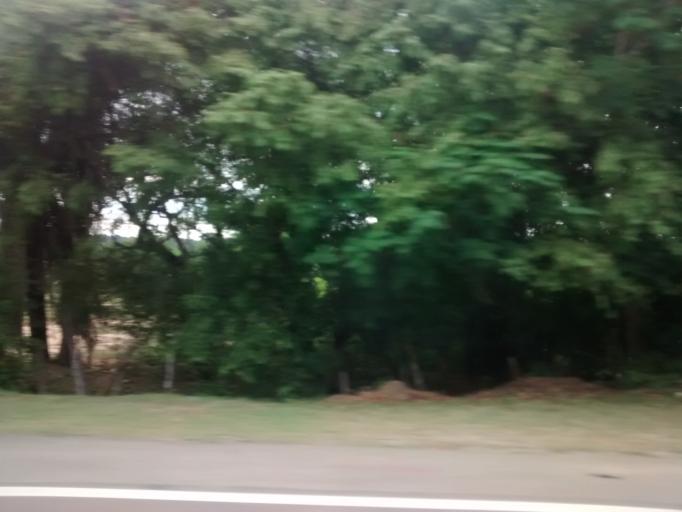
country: CO
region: Tolima
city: Melgar
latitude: 4.2193
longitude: -74.6914
